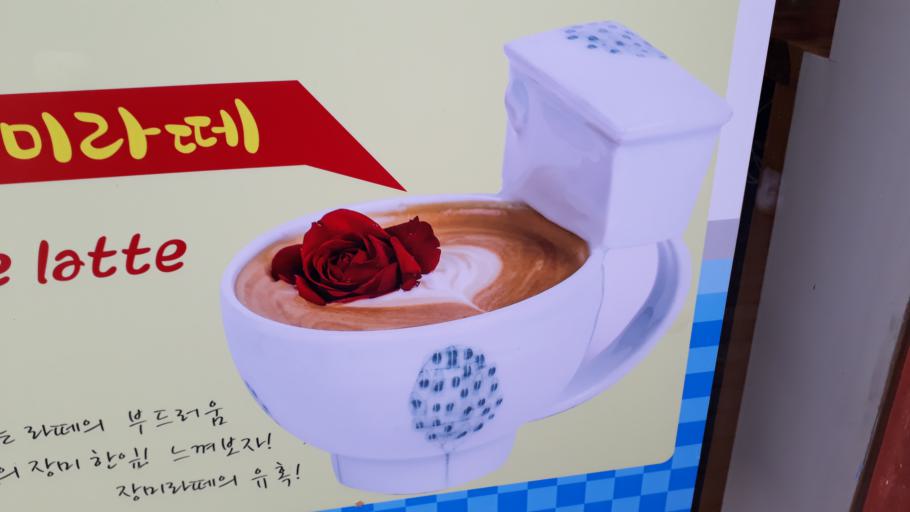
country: KR
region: Seoul
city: Seoul
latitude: 37.5744
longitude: 126.9847
